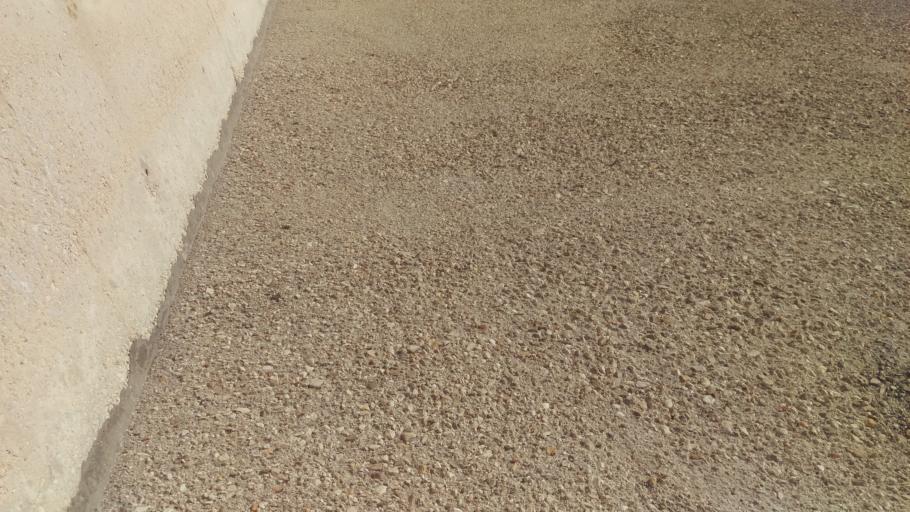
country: IT
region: Apulia
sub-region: Provincia di Brindisi
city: Materdomini
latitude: 40.6629
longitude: 17.9747
